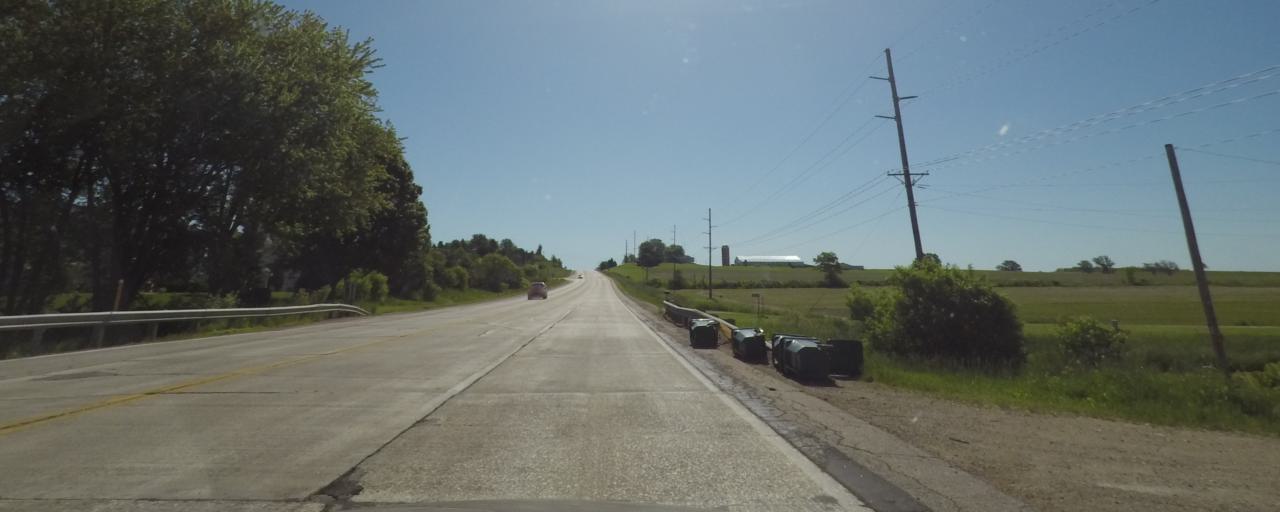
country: US
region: Wisconsin
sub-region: Fond du Lac County
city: Saint Peter
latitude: 43.7836
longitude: -88.3746
